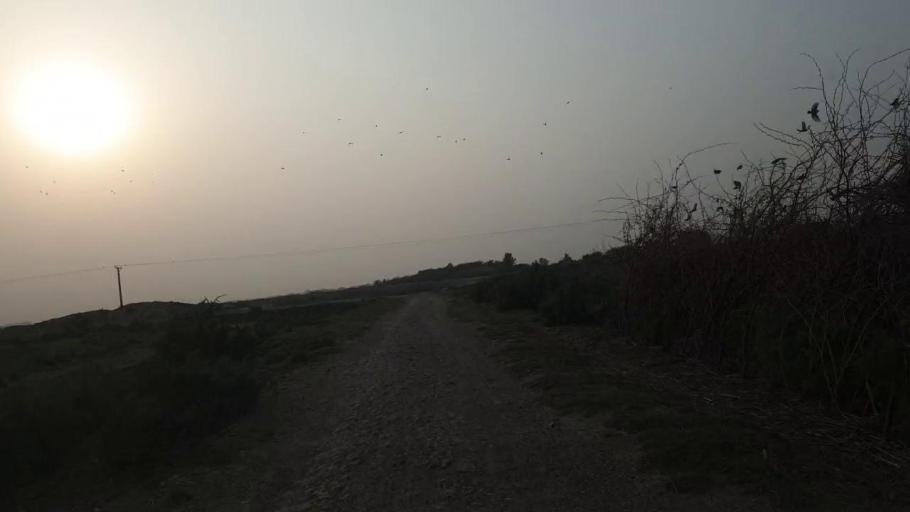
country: PK
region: Sindh
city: Mirpur Batoro
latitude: 24.6637
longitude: 68.3767
